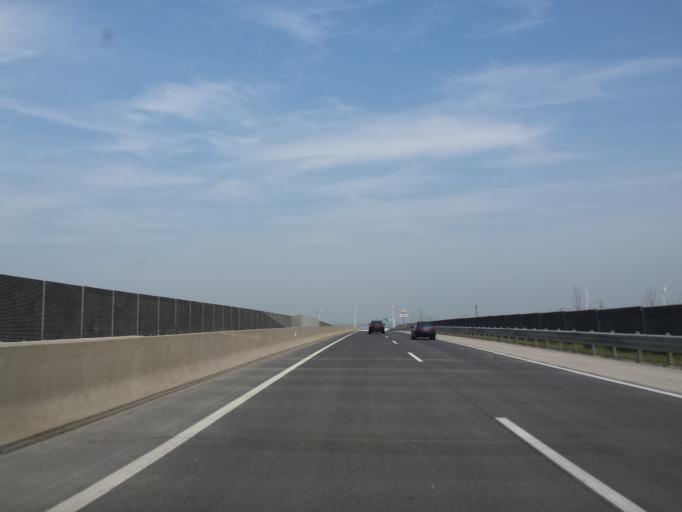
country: AT
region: Lower Austria
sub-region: Politischer Bezirk Ganserndorf
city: Aderklaa
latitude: 48.3041
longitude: 16.5099
